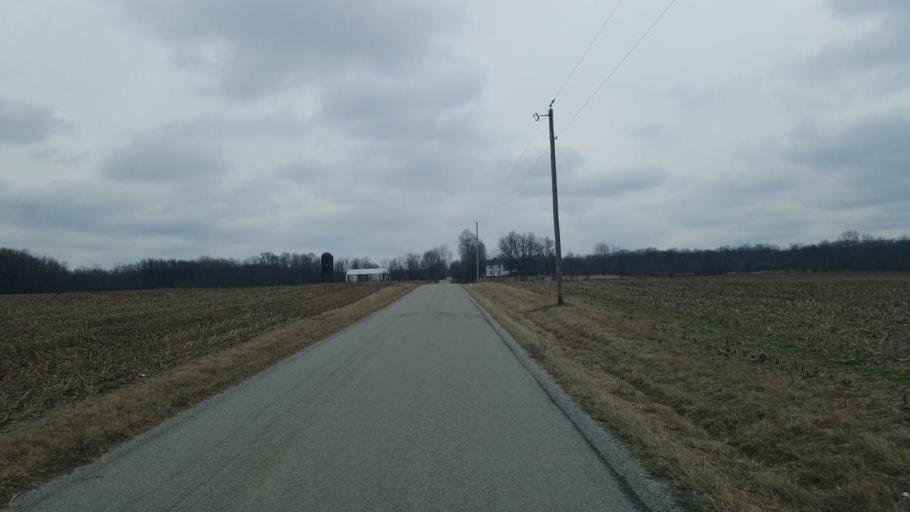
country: US
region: Ohio
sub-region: Morrow County
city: Mount Gilead
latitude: 40.6108
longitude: -82.8414
